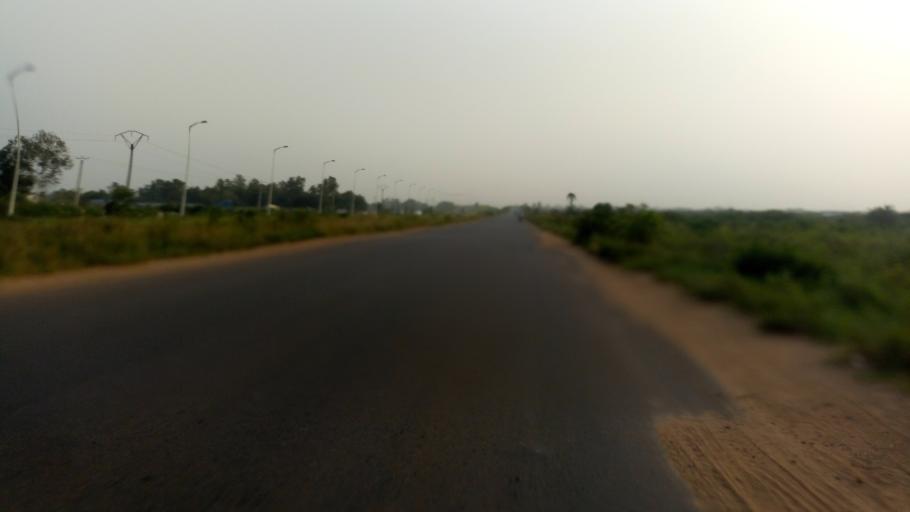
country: TG
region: Maritime
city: Tsevie
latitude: 6.3128
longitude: 1.2163
